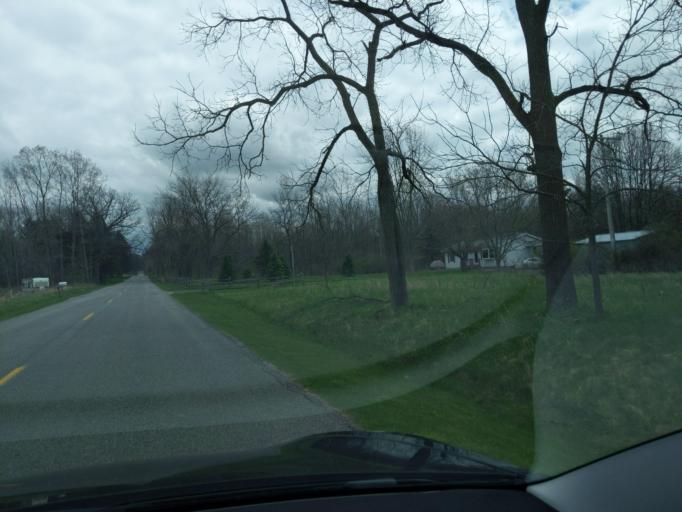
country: US
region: Michigan
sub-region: Ingham County
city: Holt
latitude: 42.5676
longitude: -84.5739
